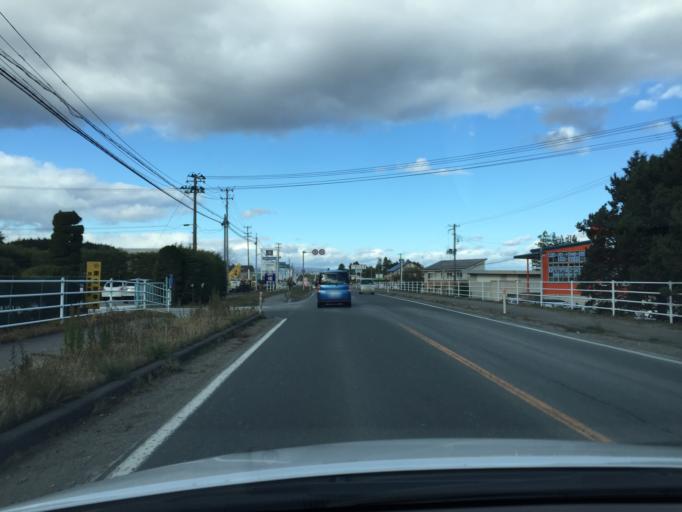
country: JP
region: Fukushima
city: Namie
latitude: 37.6209
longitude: 140.9975
